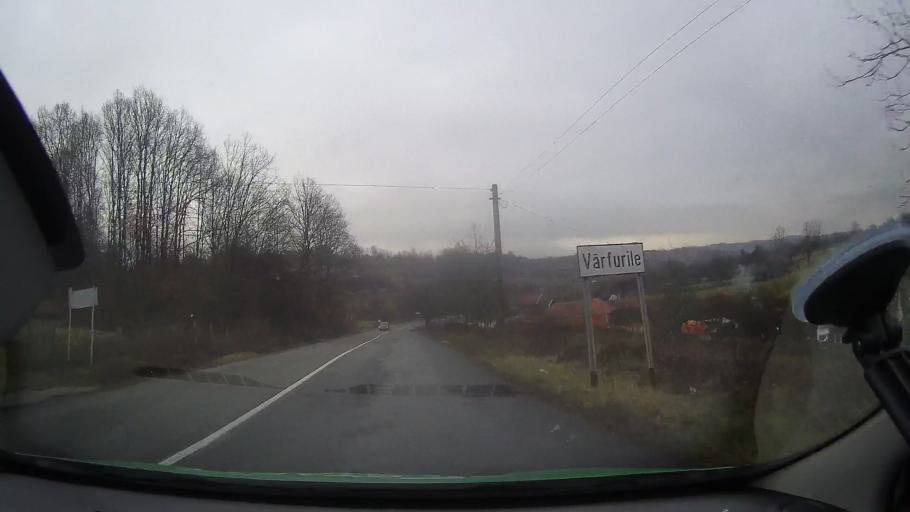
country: RO
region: Arad
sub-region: Comuna Varfurile
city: Varfurile
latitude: 46.3217
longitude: 22.5020
